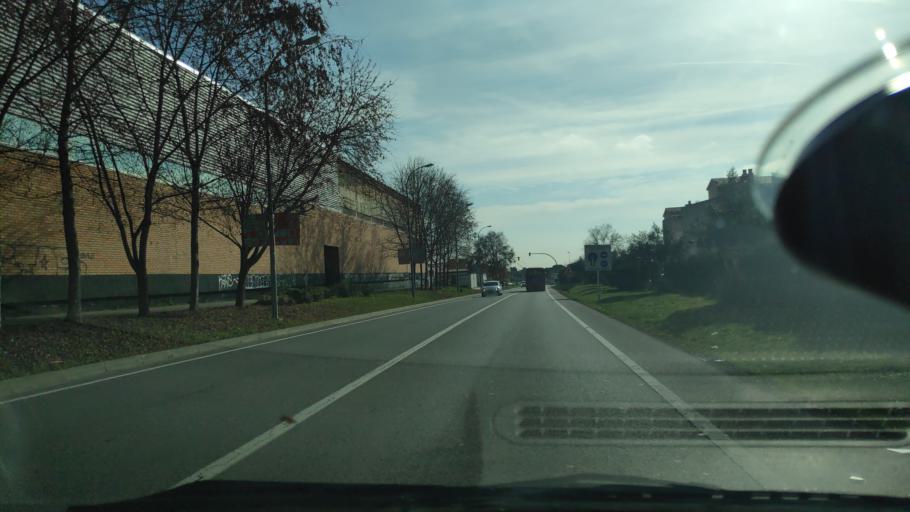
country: ES
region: Catalonia
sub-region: Provincia de Barcelona
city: Castellar del Valles
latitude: 41.6087
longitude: 2.0841
